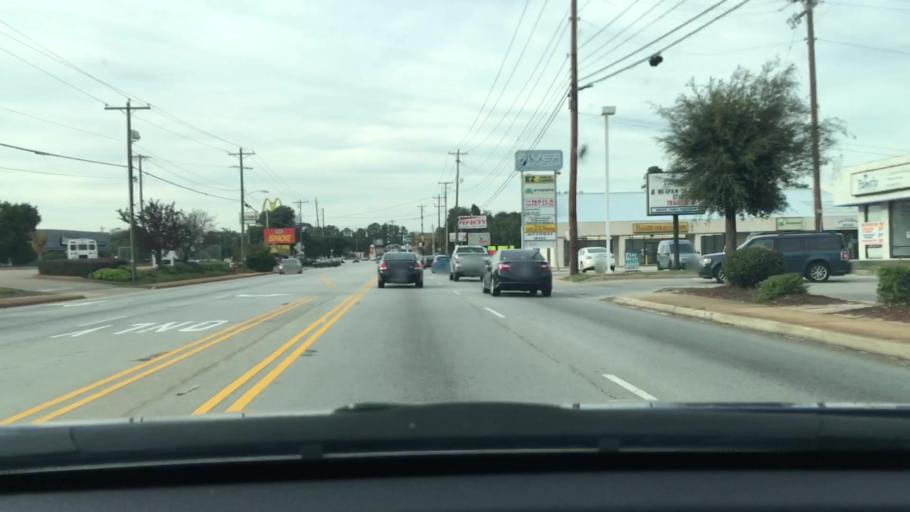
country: US
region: South Carolina
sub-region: Lexington County
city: Saint Andrews
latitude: 34.0338
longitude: -81.0884
